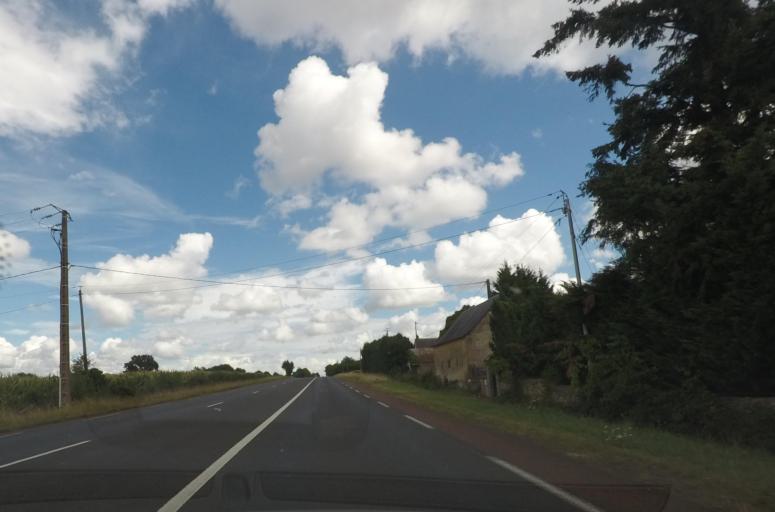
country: FR
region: Pays de la Loire
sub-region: Departement de la Sarthe
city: Clermont-Creans
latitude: 47.7382
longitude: -0.0046
